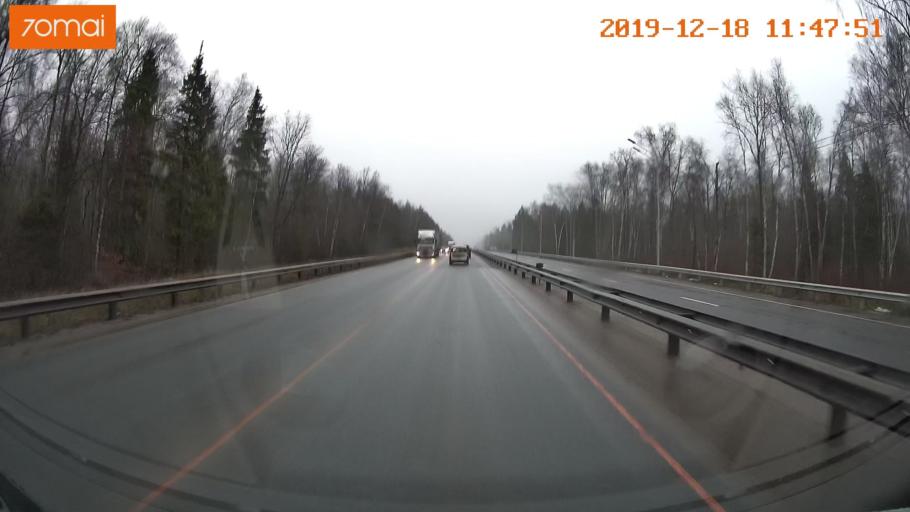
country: RU
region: Moskovskaya
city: Yershovo
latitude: 55.7619
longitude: 36.8983
